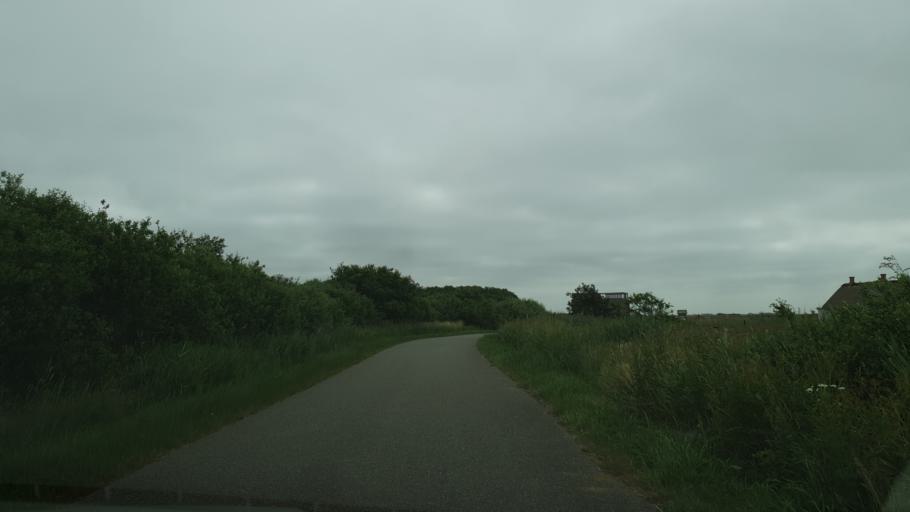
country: DK
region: Central Jutland
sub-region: Ringkobing-Skjern Kommune
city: Skjern
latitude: 55.9207
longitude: 8.4054
